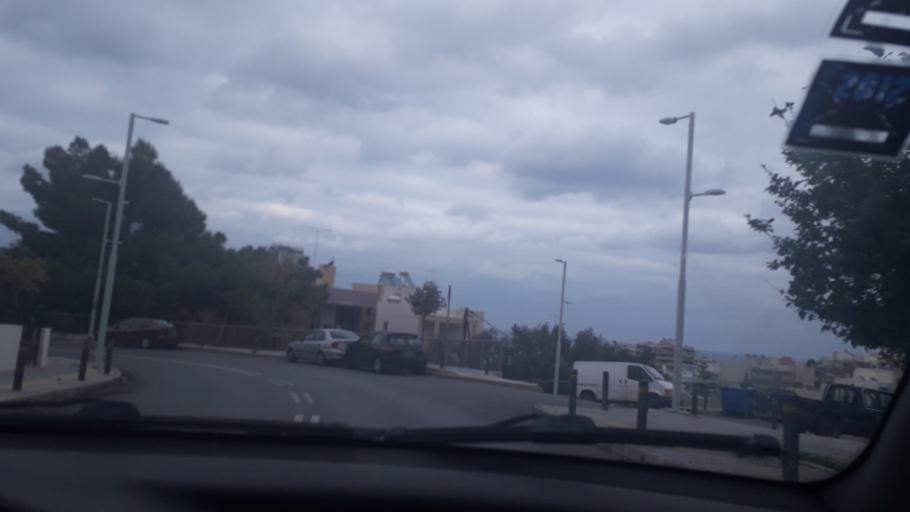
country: GR
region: Crete
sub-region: Nomos Rethymnis
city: Rethymno
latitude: 35.3592
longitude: 24.4765
